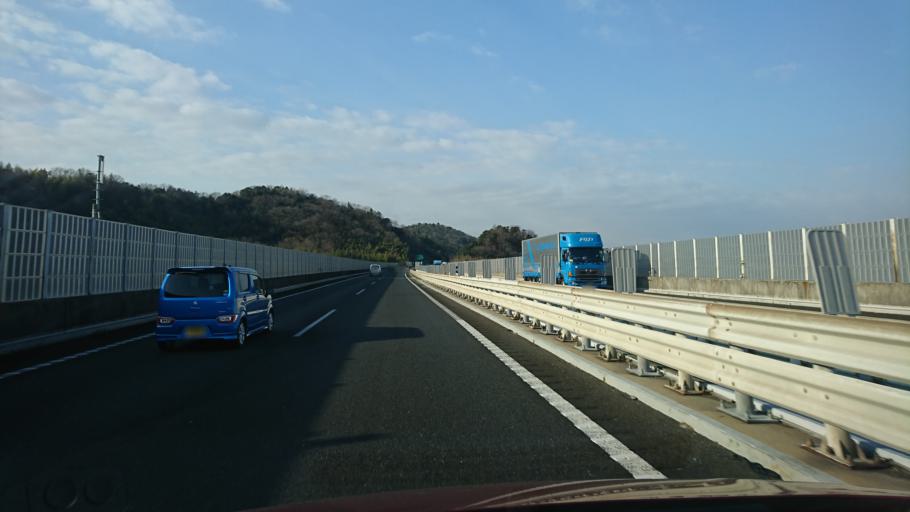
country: JP
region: Hyogo
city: Tatsunocho-tominaga
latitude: 34.8498
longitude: 134.5317
